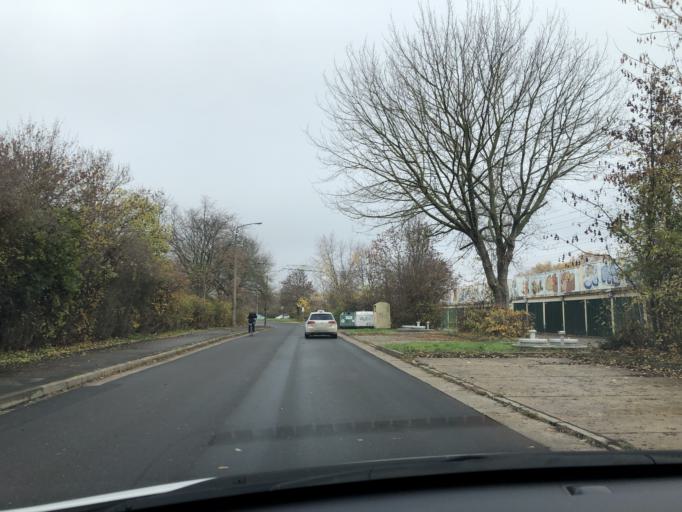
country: DE
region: Saxony-Anhalt
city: Halle Neustadt
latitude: 51.4782
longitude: 11.9436
